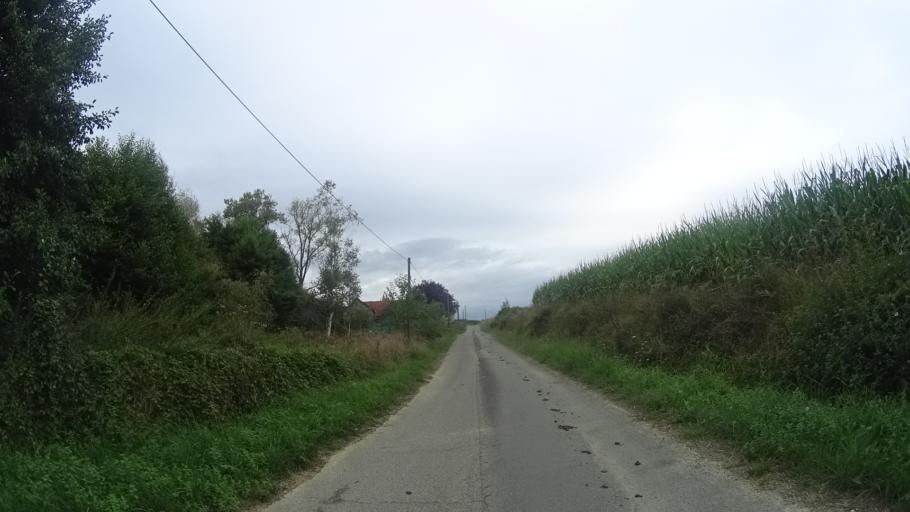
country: FR
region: Aquitaine
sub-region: Departement des Pyrenees-Atlantiques
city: Orthez
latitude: 43.4899
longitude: -0.7124
